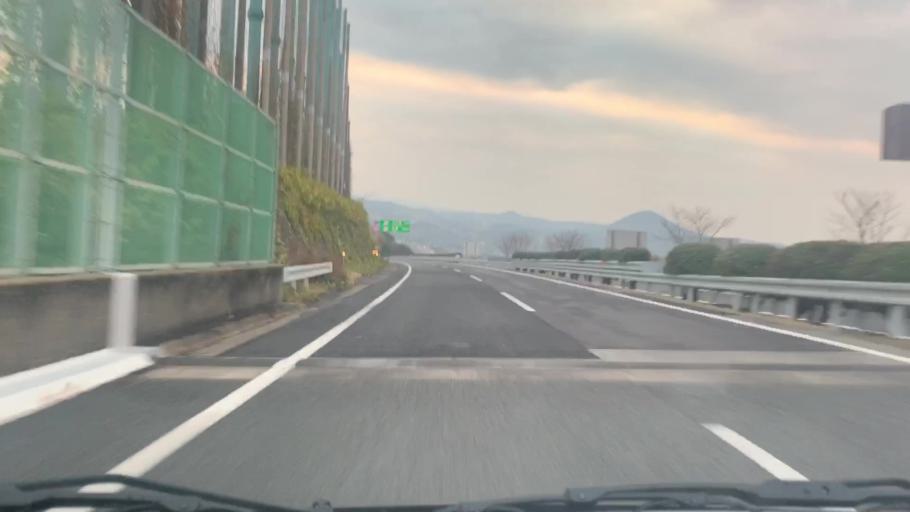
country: JP
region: Saga Prefecture
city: Ureshinomachi-shimojuku
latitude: 33.0299
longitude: 129.9305
